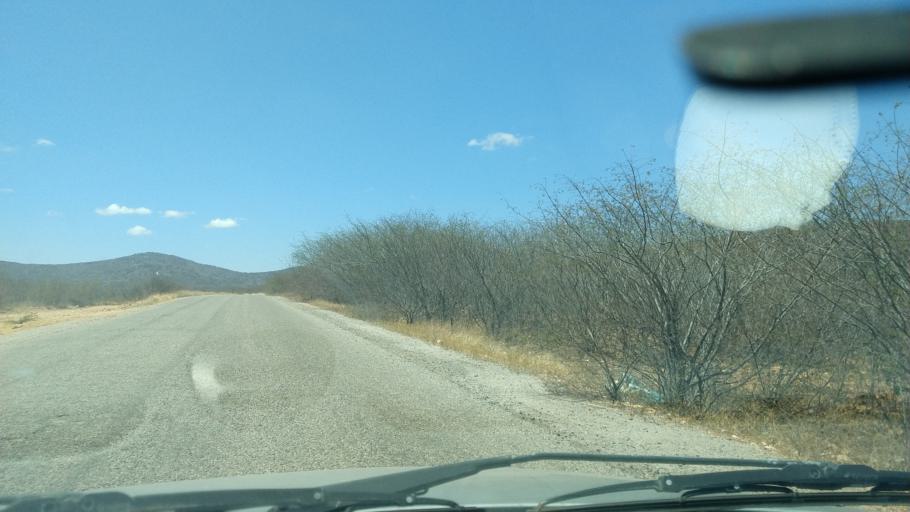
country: BR
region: Rio Grande do Norte
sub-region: Sao Tome
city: Sao Tome
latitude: -5.9721
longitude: -36.1352
